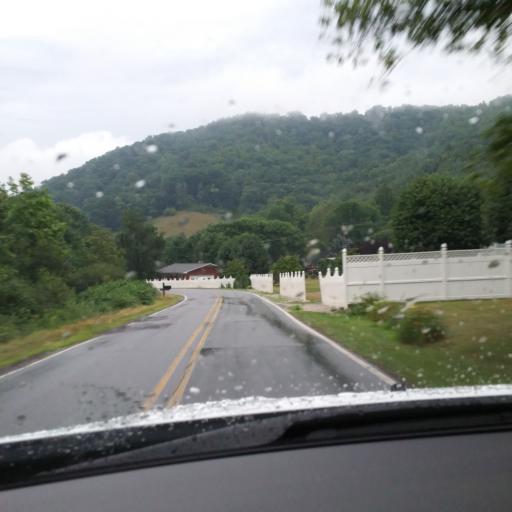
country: US
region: North Carolina
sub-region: Yancey County
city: Burnsville
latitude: 35.8917
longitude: -82.2823
